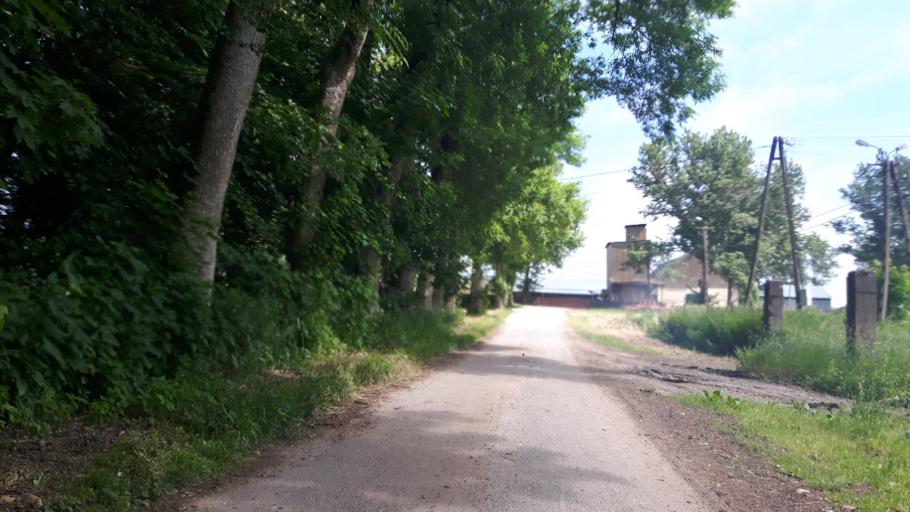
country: PL
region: West Pomeranian Voivodeship
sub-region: Powiat slawienski
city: Darlowo
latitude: 54.4704
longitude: 16.4688
